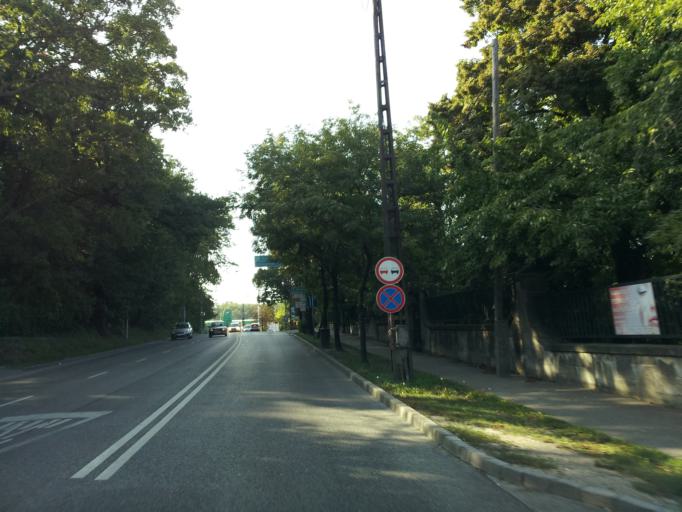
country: HU
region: Pest
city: Budakeszi
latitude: 47.5364
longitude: 18.9701
